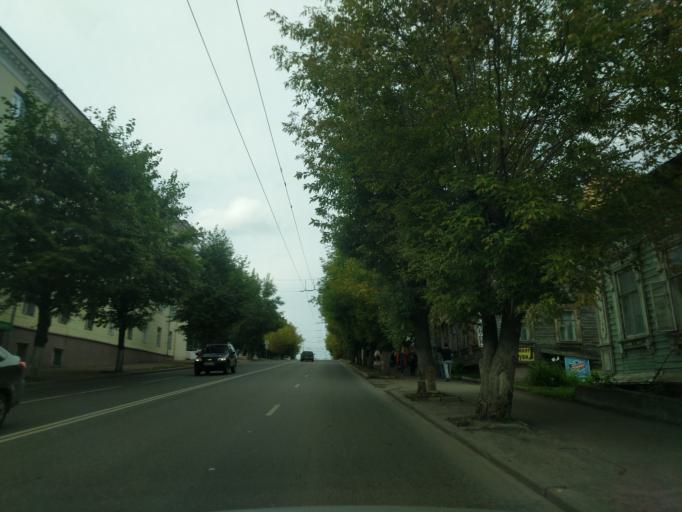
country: RU
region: Kirov
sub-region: Kirovo-Chepetskiy Rayon
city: Kirov
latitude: 58.5917
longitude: 49.6690
